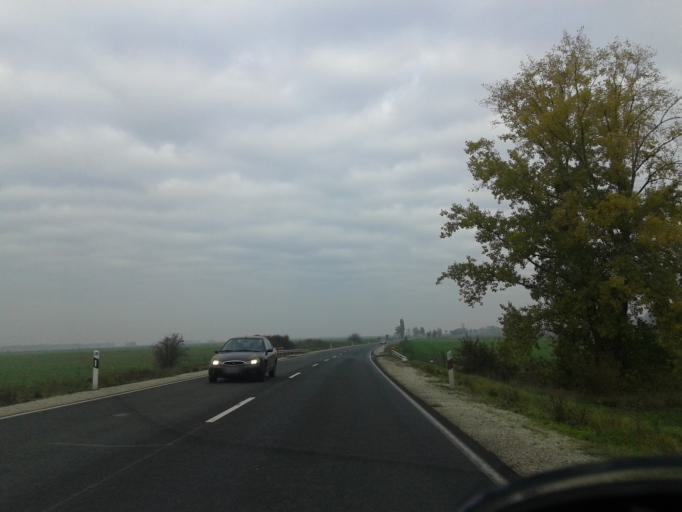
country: HU
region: Fejer
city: Ercsi
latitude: 47.2830
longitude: 18.8733
